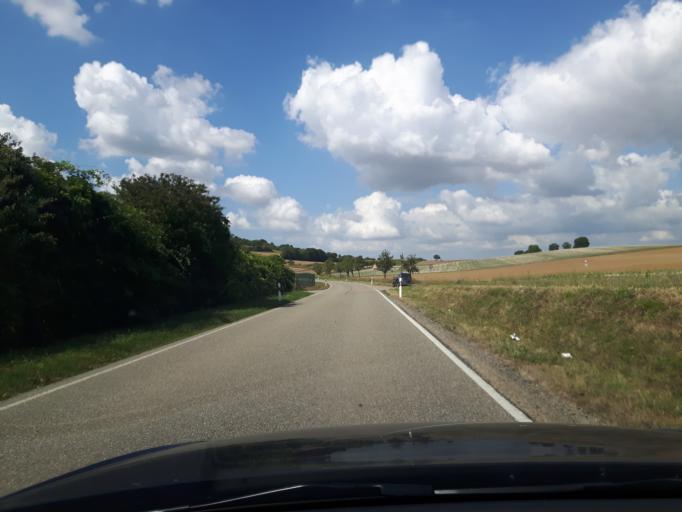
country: DE
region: Baden-Wuerttemberg
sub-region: Karlsruhe Region
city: Sinsheim
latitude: 49.2155
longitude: 8.8962
